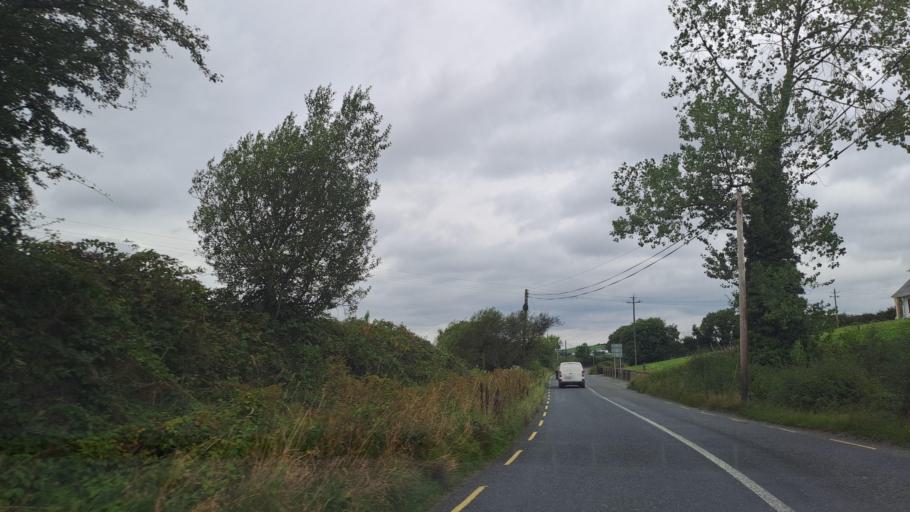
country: IE
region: Ulster
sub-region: An Cabhan
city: Bailieborough
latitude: 53.9725
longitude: -6.9126
